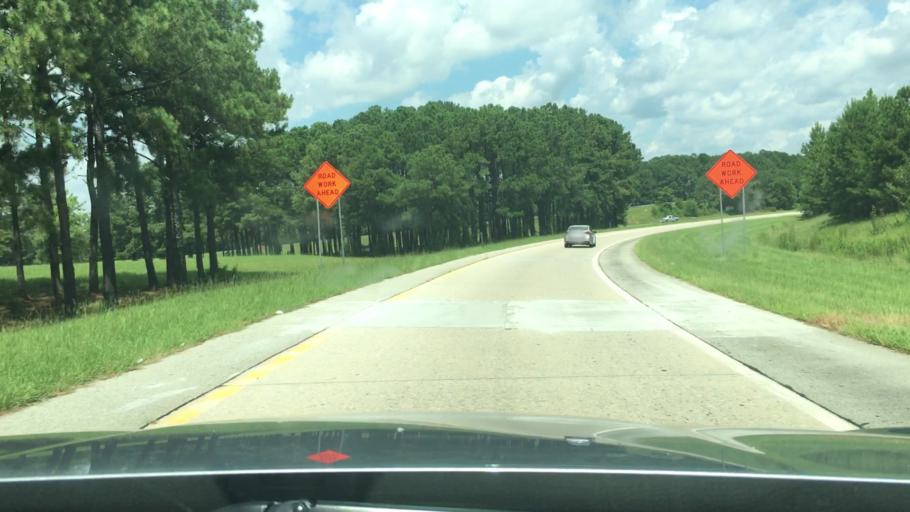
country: US
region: South Carolina
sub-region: Florence County
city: Florence
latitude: 34.1926
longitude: -79.8412
